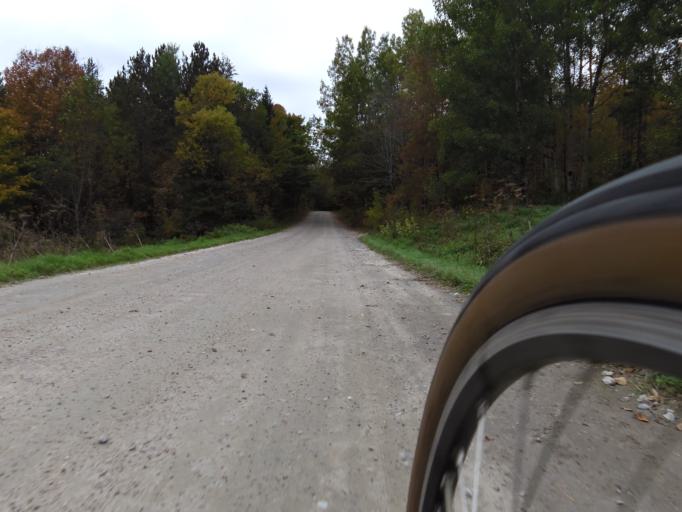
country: CA
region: Quebec
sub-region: Outaouais
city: Wakefield
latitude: 45.6044
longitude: -76.0150
